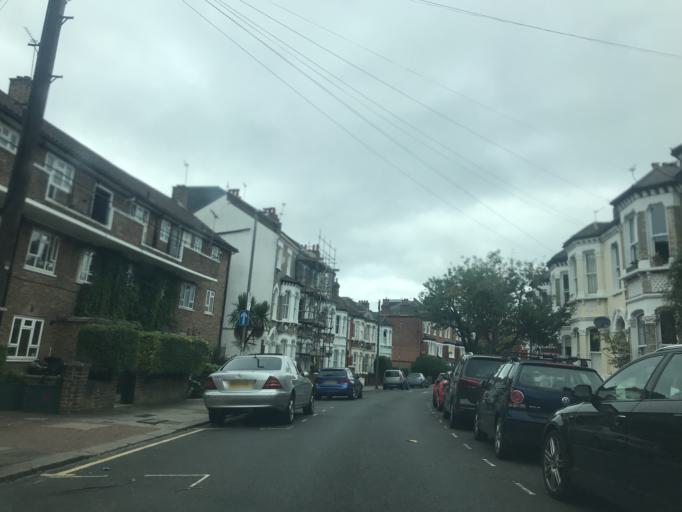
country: GB
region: England
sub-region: Greater London
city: Battersea
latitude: 51.4614
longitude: -0.1644
